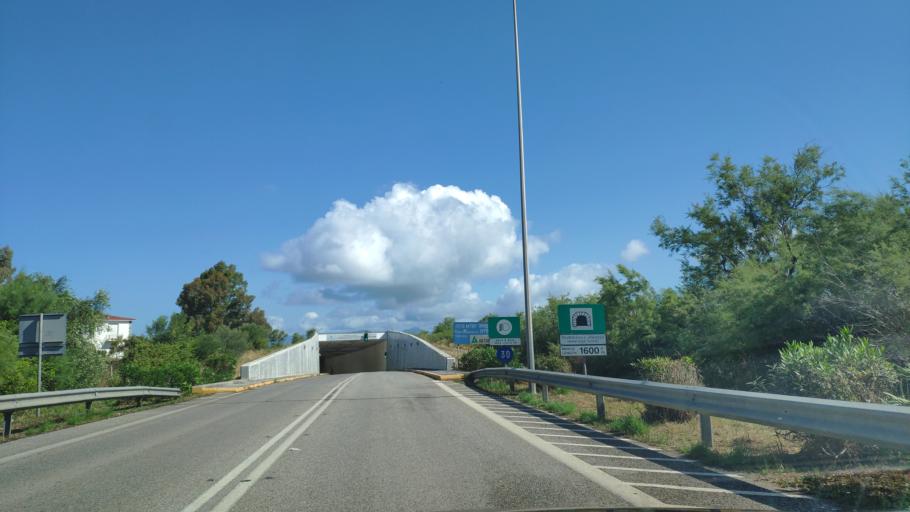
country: GR
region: Epirus
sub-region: Nomos Prevezis
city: Preveza
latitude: 38.9430
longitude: 20.7645
